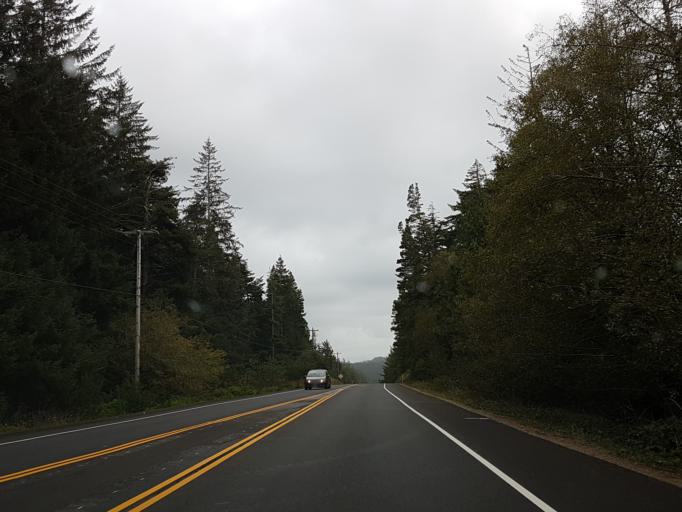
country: US
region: Oregon
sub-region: Lane County
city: Dunes City
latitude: 43.8947
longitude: -124.1182
